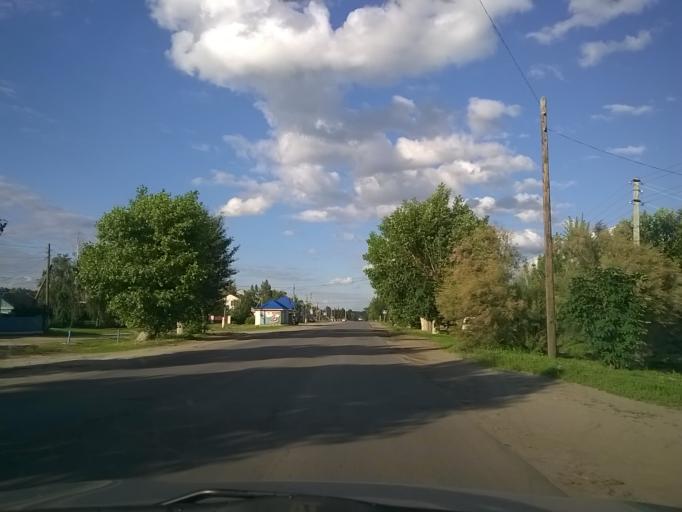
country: RU
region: Volgograd
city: Uryupinsk
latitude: 50.8174
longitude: 42.0324
